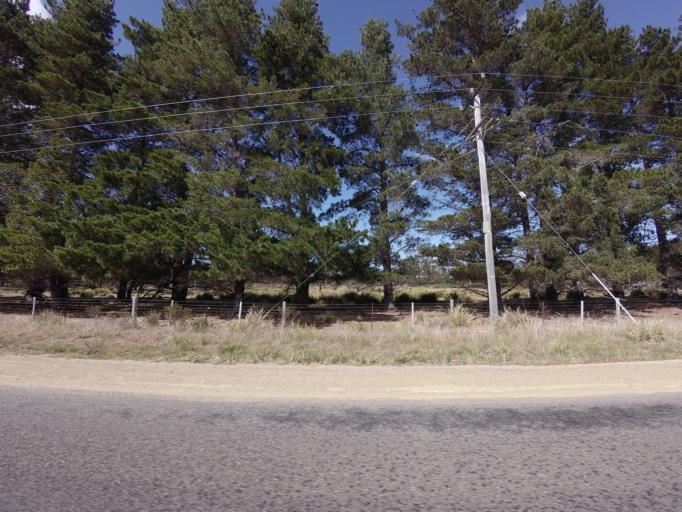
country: AU
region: Tasmania
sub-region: Break O'Day
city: St Helens
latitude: -41.9455
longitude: 148.2069
